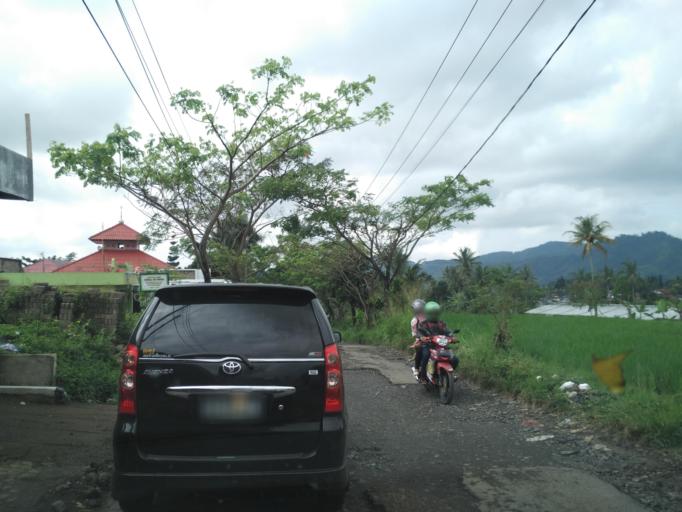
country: ID
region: West Java
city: Ciranjang-hilir
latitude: -6.7198
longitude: 107.0751
